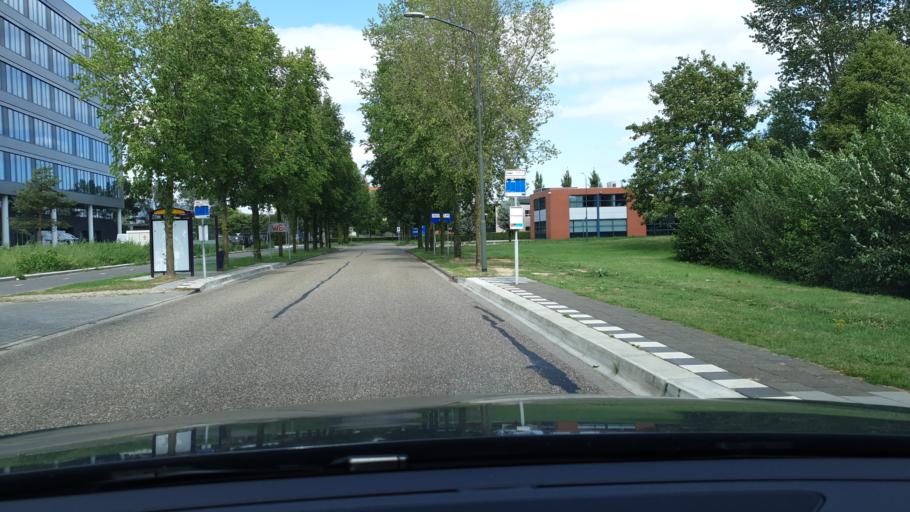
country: NL
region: North Brabant
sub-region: Gemeente Son en Breugel
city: Son
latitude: 51.4979
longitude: 5.4596
